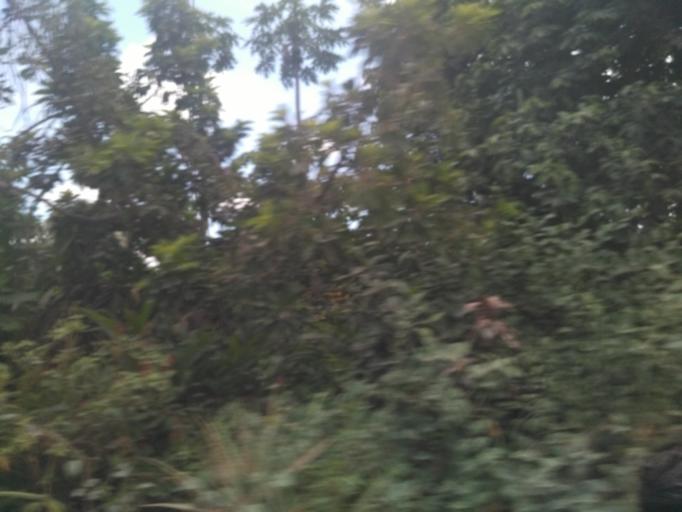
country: TZ
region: Dar es Salaam
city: Dar es Salaam
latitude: -6.8495
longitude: 39.2684
